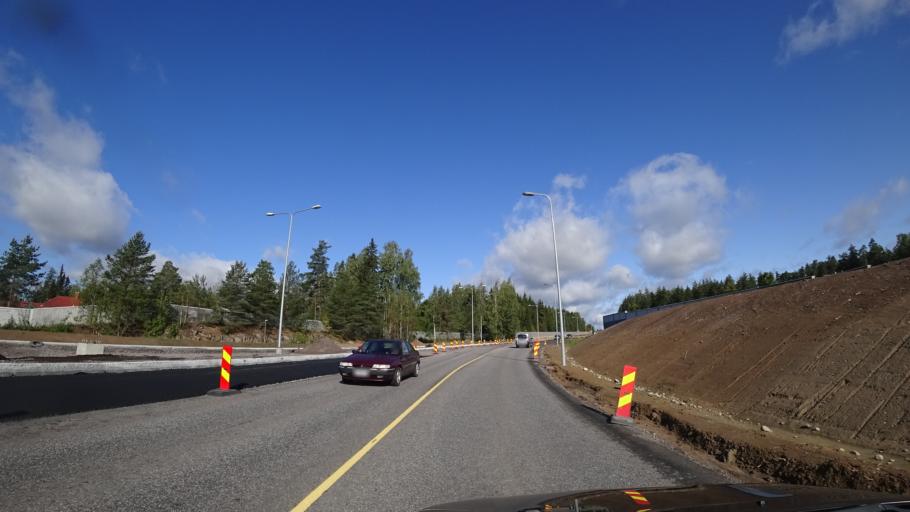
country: FI
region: Uusimaa
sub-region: Helsinki
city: Tuusula
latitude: 60.4066
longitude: 25.0073
